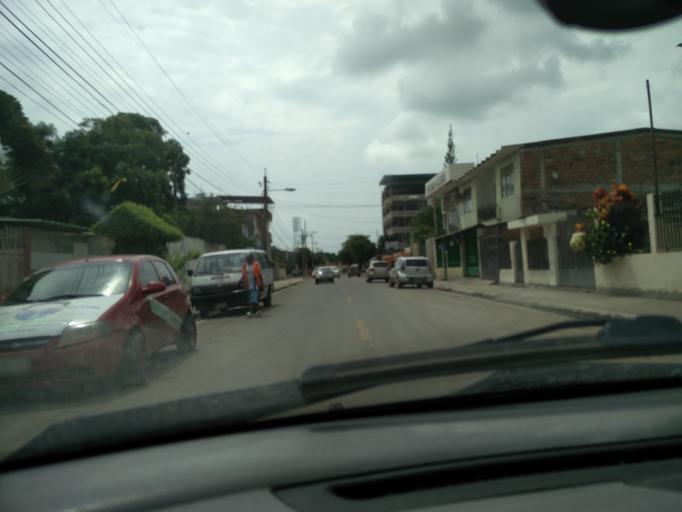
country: EC
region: Manabi
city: Portoviejo
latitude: -1.0516
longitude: -80.4526
